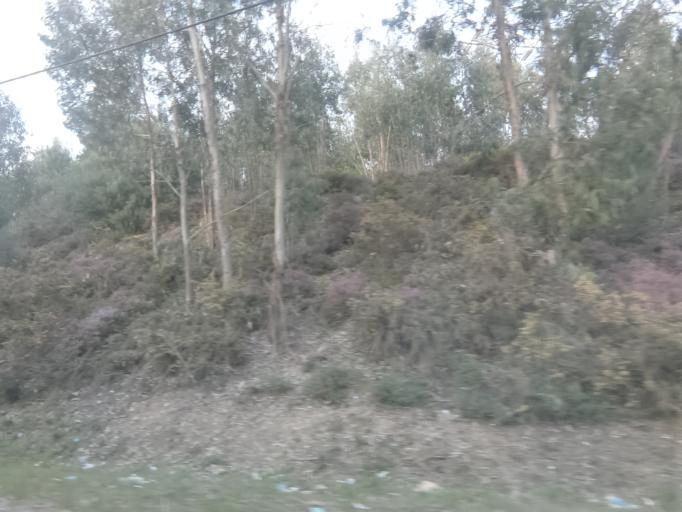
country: PT
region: Porto
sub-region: Valongo
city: Valongo
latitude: 41.1974
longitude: -8.5224
